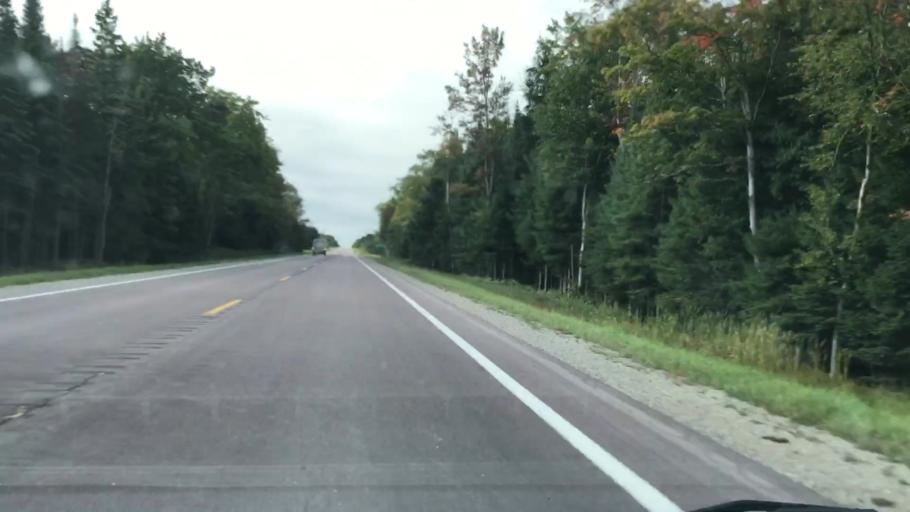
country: US
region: Michigan
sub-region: Luce County
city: Newberry
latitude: 46.2919
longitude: -85.5696
